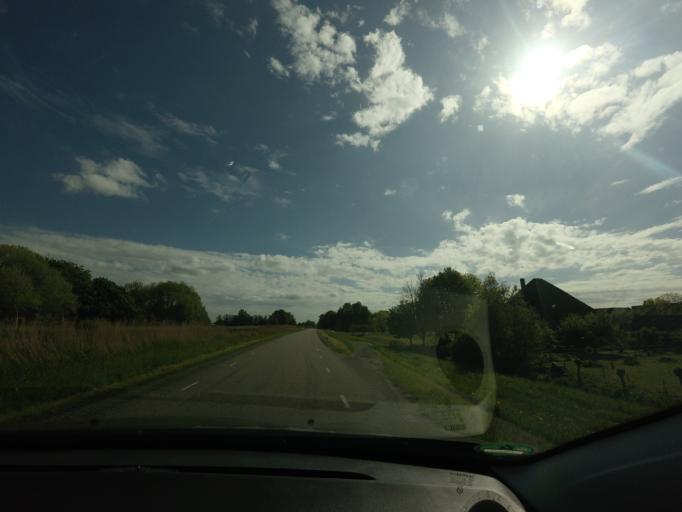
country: NL
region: North Holland
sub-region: Gemeente Heerhugowaard
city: Heerhugowaard
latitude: 52.6721
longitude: 4.8728
